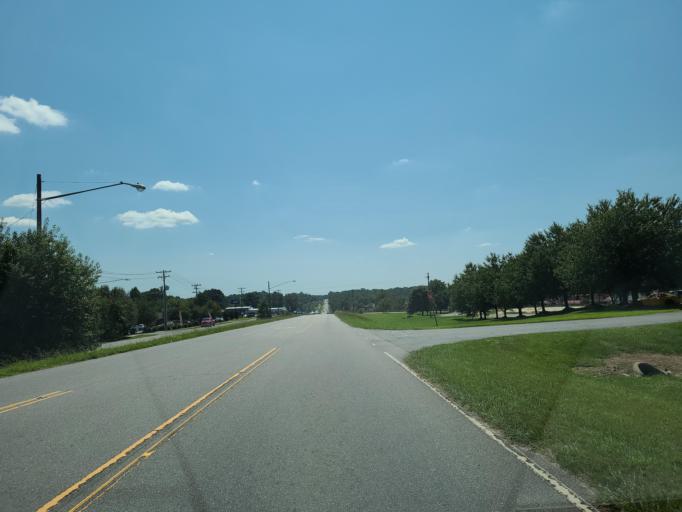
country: US
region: North Carolina
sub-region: Lincoln County
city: Lincolnton
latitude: 35.4934
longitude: -81.2463
